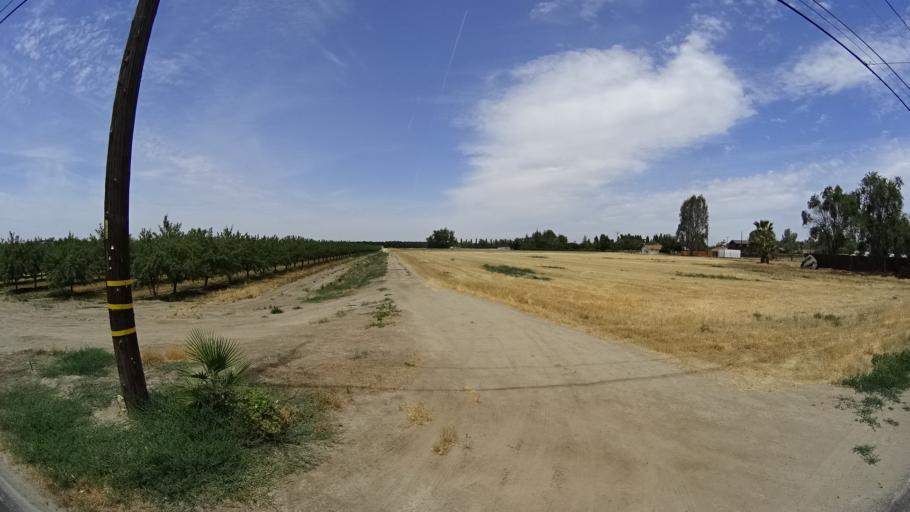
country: US
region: California
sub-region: Kings County
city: Armona
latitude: 36.3170
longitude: -119.7134
